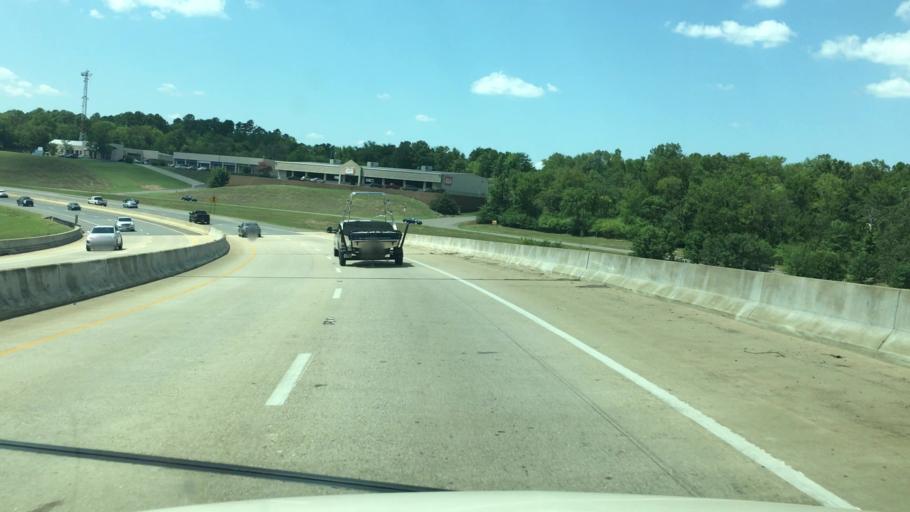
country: US
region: Arkansas
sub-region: Garland County
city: Rockwell
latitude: 34.4698
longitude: -93.0890
